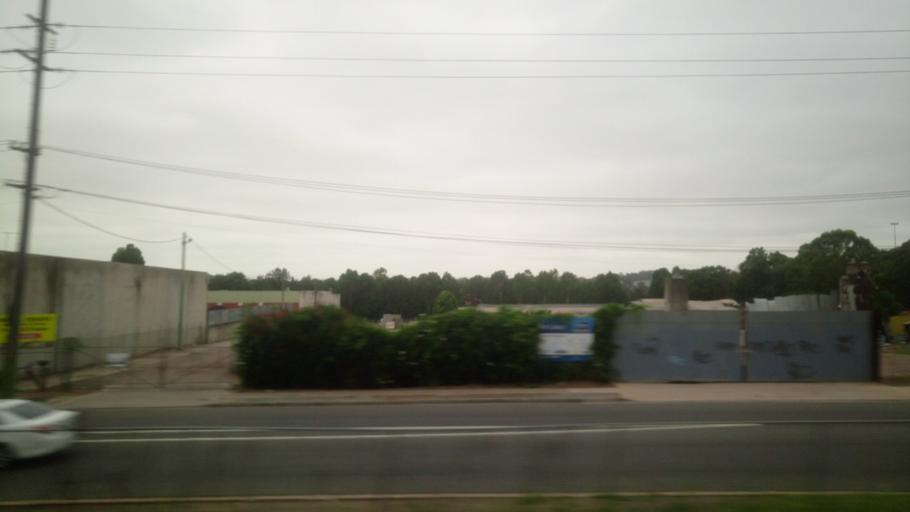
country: AU
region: New South Wales
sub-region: Holroyd
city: Girraween
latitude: -33.7797
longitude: 150.9470
